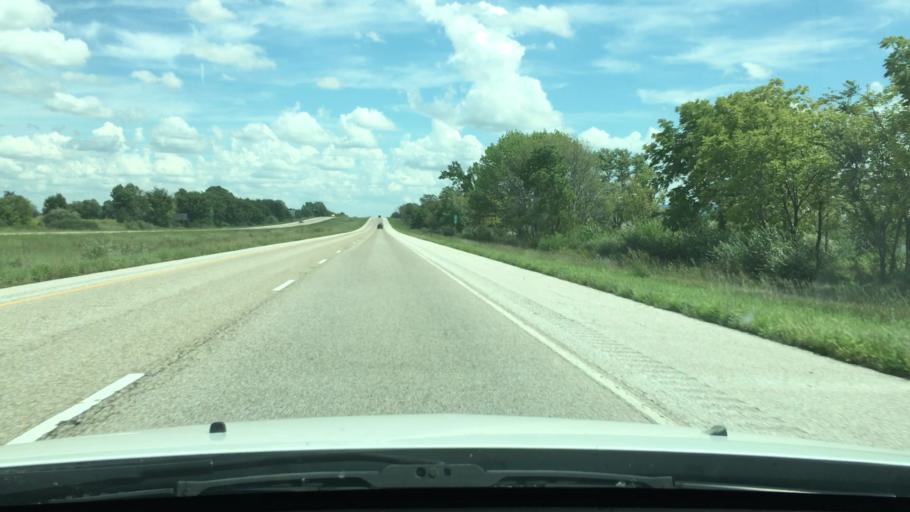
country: US
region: Illinois
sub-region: Scott County
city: Winchester
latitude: 39.6809
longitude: -90.4384
